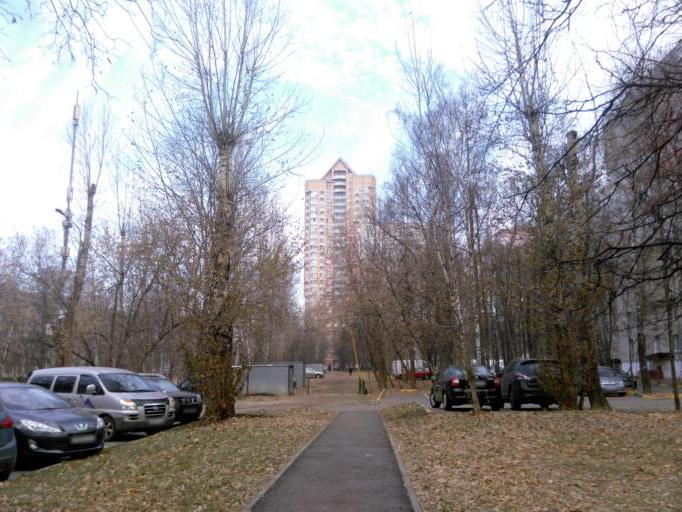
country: RU
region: Moscow
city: Troparevo
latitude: 55.6700
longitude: 37.5089
